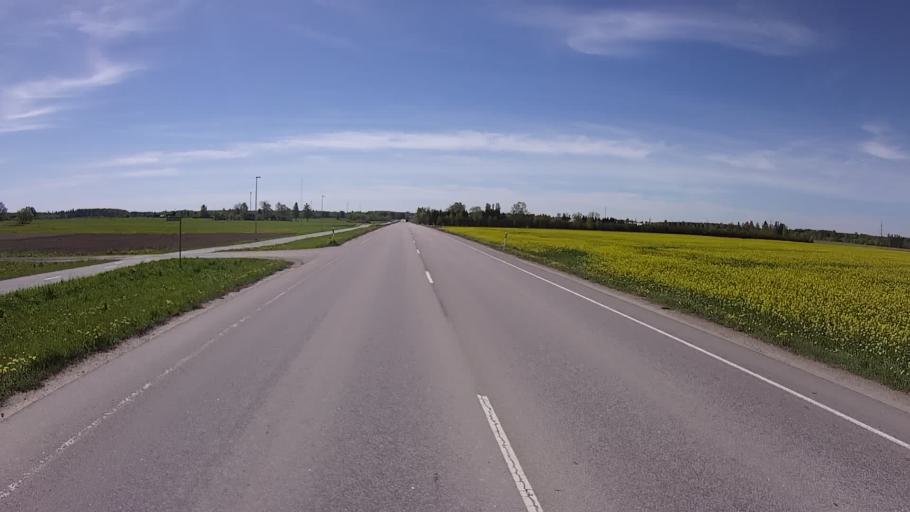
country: EE
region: Polvamaa
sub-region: Polva linn
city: Polva
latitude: 58.0844
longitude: 27.0908
